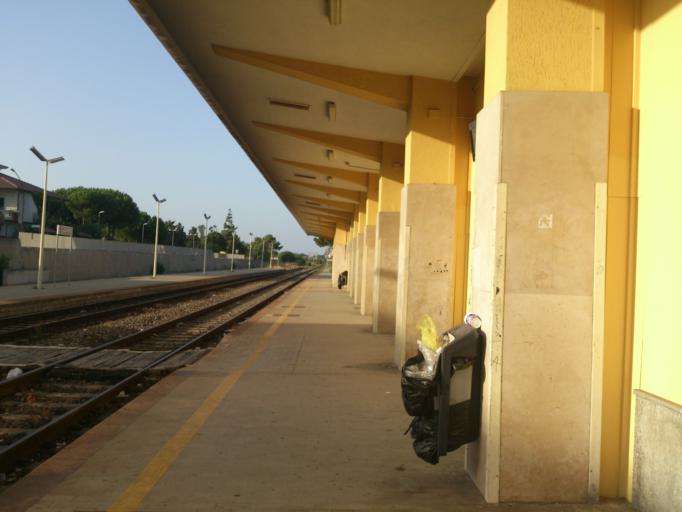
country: IT
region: Calabria
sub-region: Provincia di Reggio Calabria
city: Monasterace Marina
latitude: 38.4374
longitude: 16.5745
